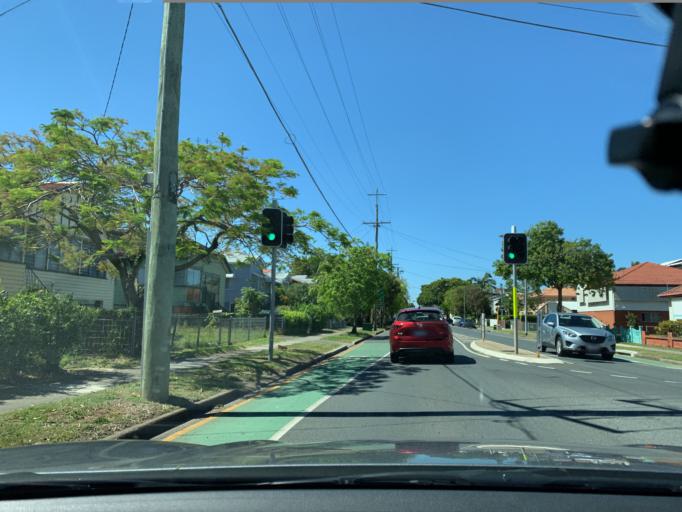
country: AU
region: Queensland
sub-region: Brisbane
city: Ascot
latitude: -27.4338
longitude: 153.0713
